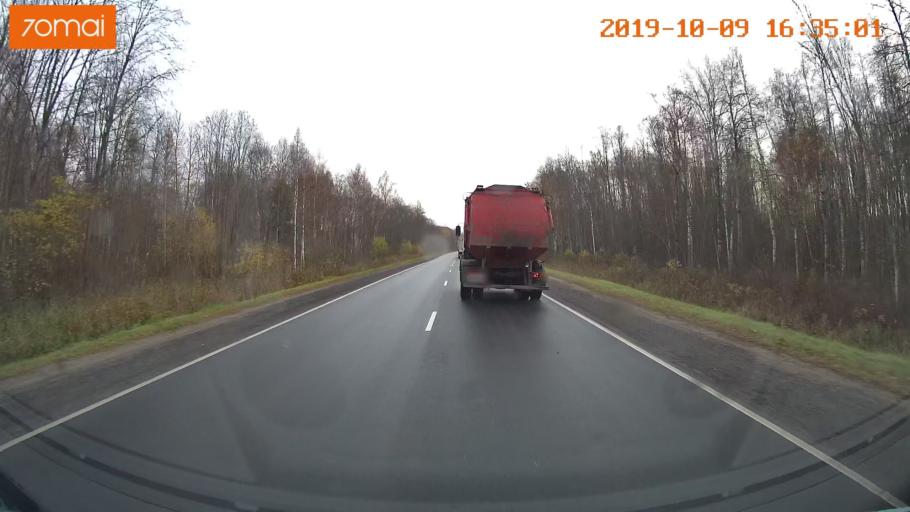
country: RU
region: Kostroma
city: Oktyabr'skiy
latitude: 57.5602
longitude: 40.9970
